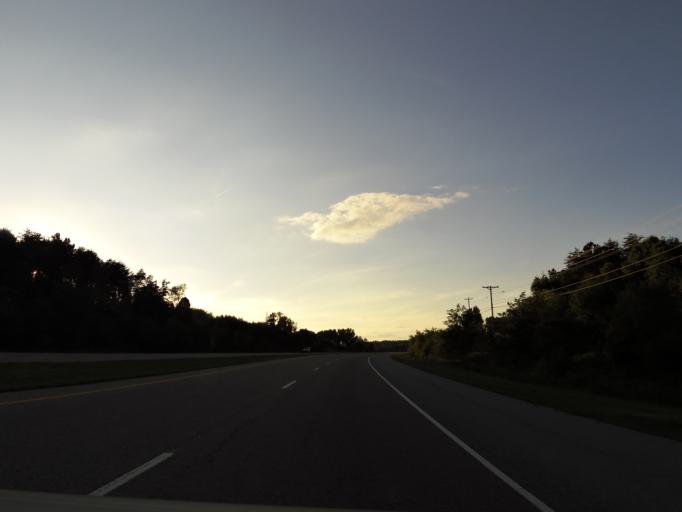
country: US
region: Tennessee
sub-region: Loudon County
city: Lenoir City
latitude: 35.7449
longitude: -84.2131
